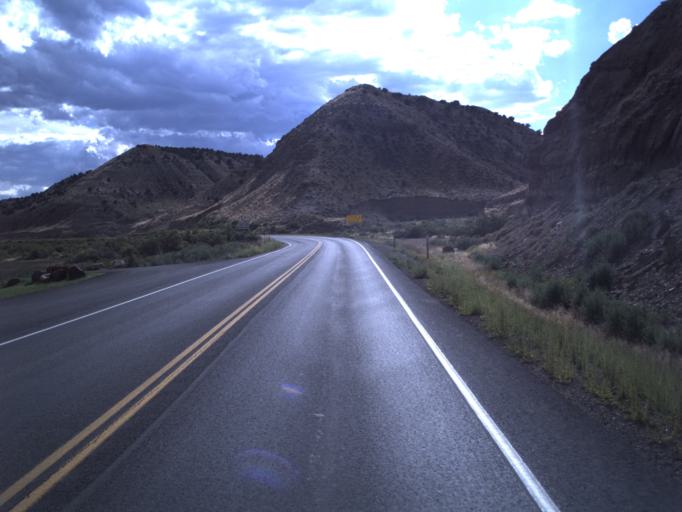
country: US
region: Utah
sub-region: Duchesne County
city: Duchesne
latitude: 40.1556
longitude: -110.4094
